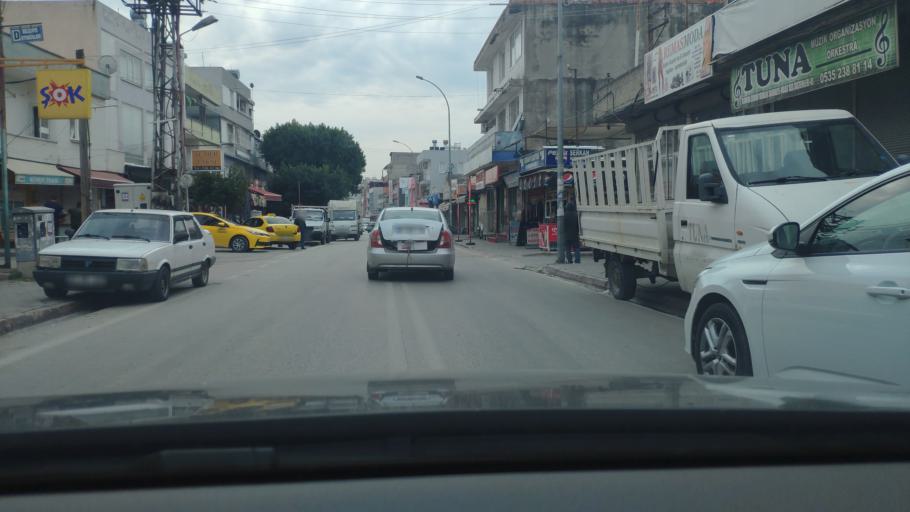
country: TR
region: Adana
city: Adana
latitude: 37.0143
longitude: 35.3146
